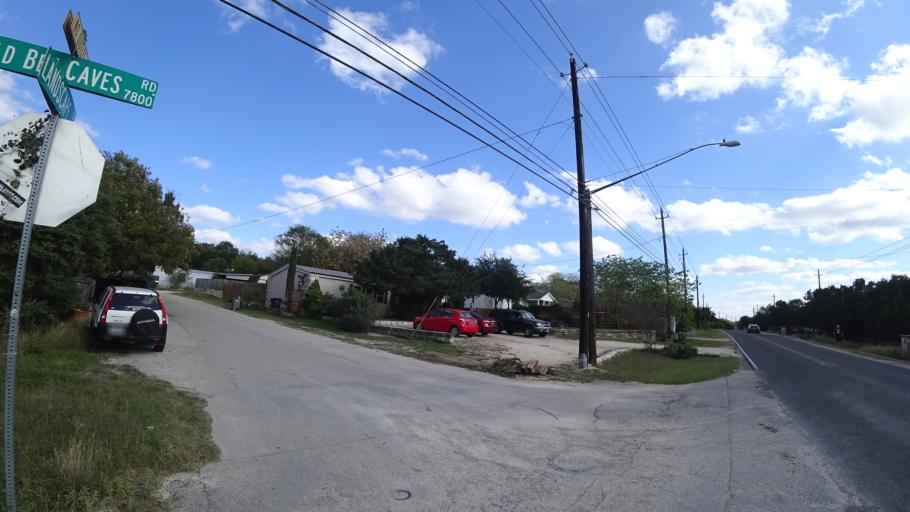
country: US
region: Texas
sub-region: Travis County
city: Barton Creek
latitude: 30.2455
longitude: -97.8812
